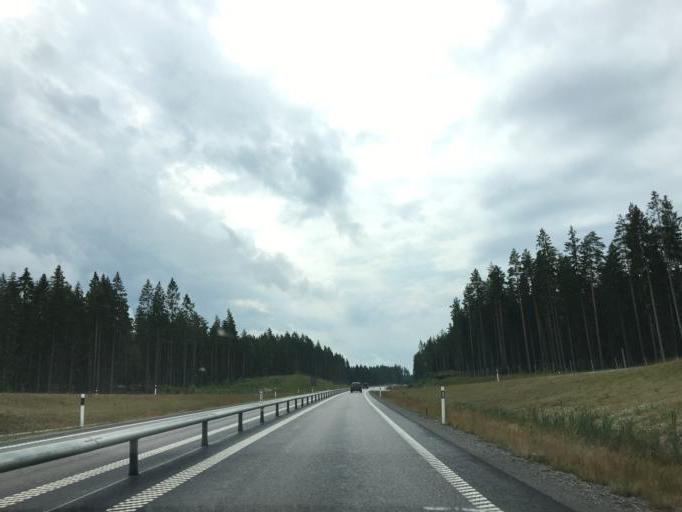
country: SE
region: Soedermanland
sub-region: Katrineholms Kommun
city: Katrineholm
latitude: 58.9935
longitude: 16.2609
